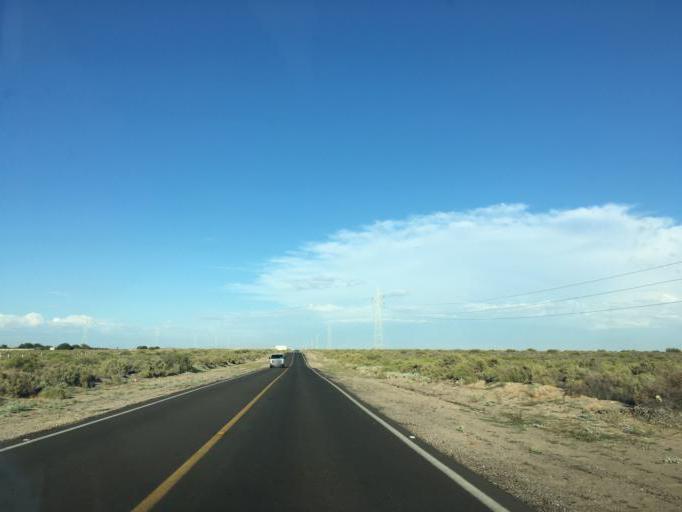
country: MX
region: Sonora
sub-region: Puerto Penasco
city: Puerto Penasco
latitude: 31.3131
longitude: -113.4934
